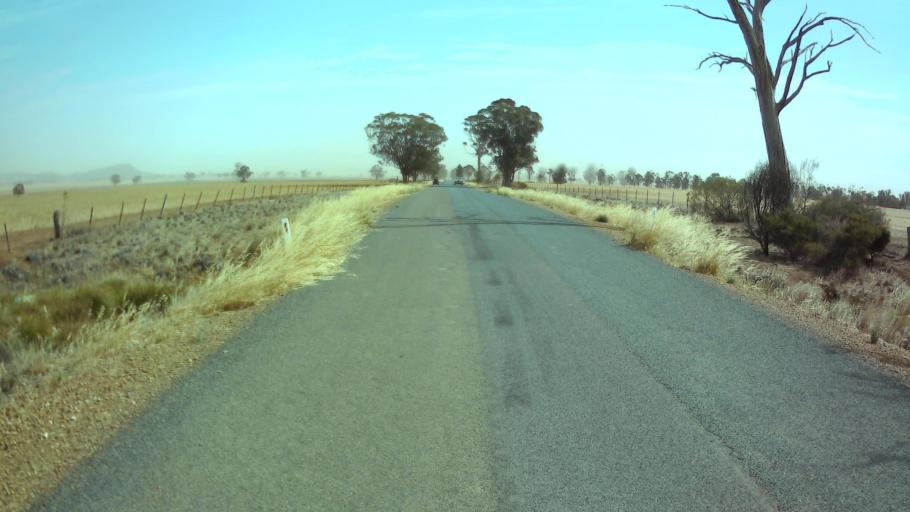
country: AU
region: New South Wales
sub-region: Weddin
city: Grenfell
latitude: -33.7708
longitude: 147.9868
